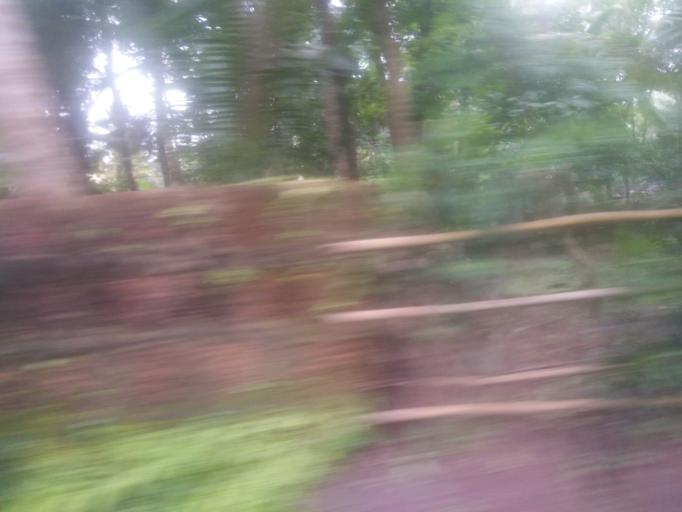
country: IN
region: Goa
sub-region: South Goa
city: Varca
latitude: 15.2198
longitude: 73.9527
